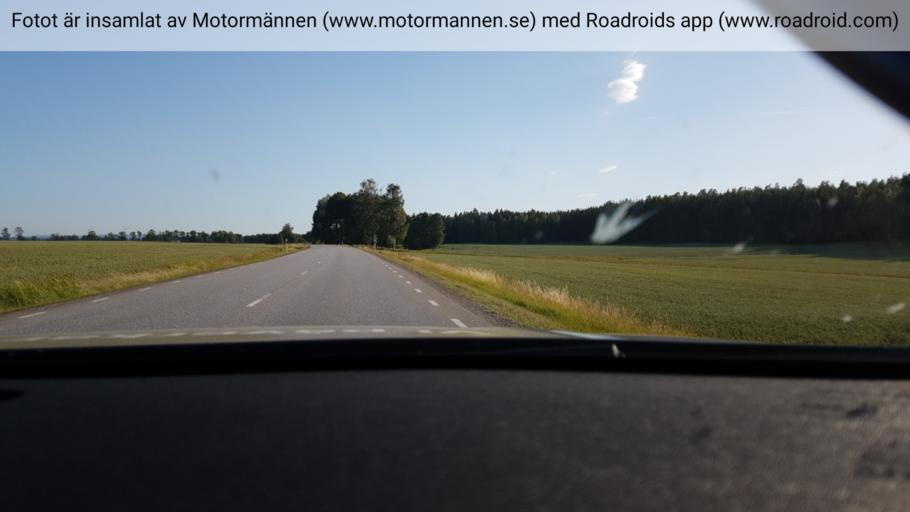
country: SE
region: Vaestra Goetaland
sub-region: Toreboda Kommun
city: Toereboda
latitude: 58.6395
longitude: 14.0307
